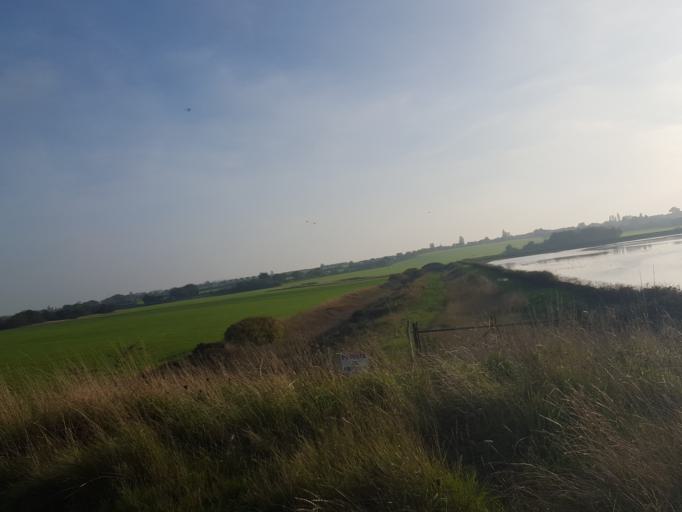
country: GB
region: England
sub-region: Essex
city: Walton-on-the-Naze
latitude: 51.8612
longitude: 1.2529
